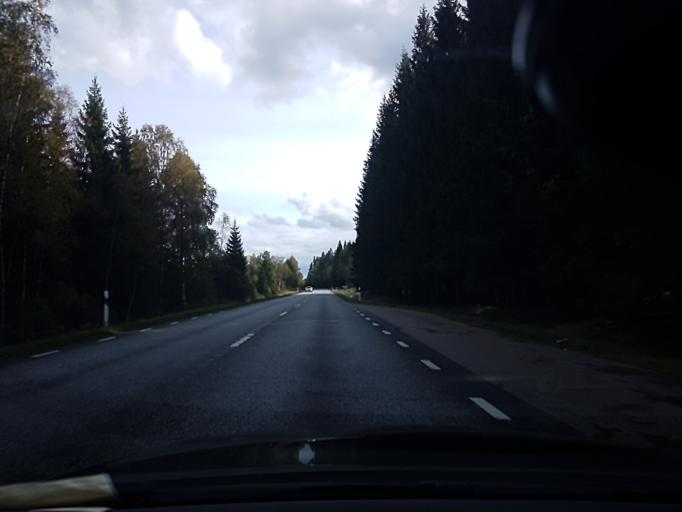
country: SE
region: Joenkoeping
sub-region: Varnamo Kommun
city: Bredaryd
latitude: 57.1925
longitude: 13.7212
